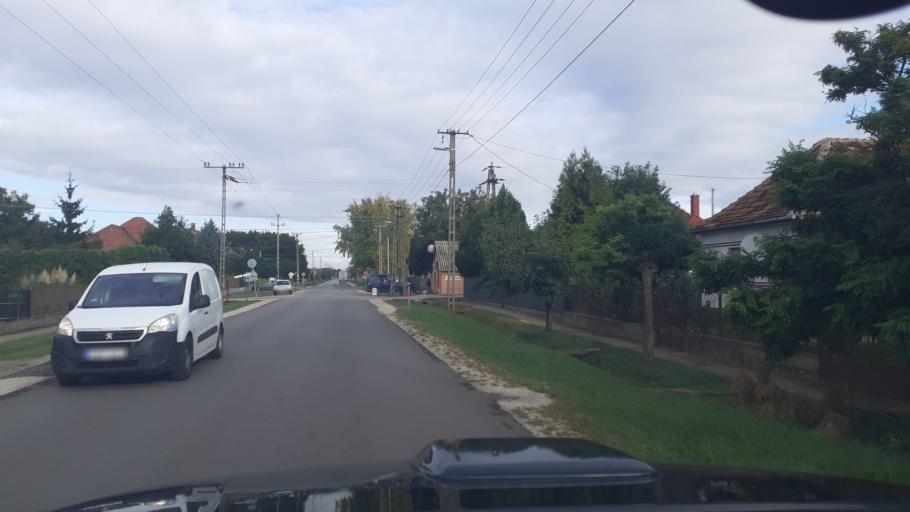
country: HU
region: Fejer
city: dunaujvaros
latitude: 46.9537
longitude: 18.8544
